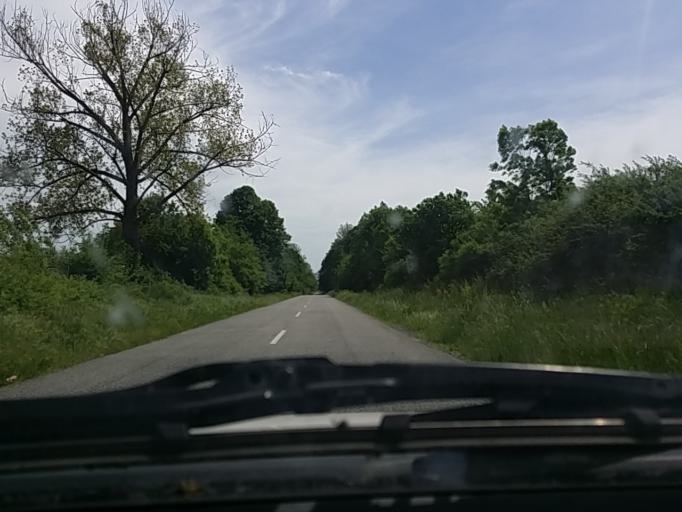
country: HU
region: Baranya
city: Sellye
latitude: 45.9191
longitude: 17.6661
